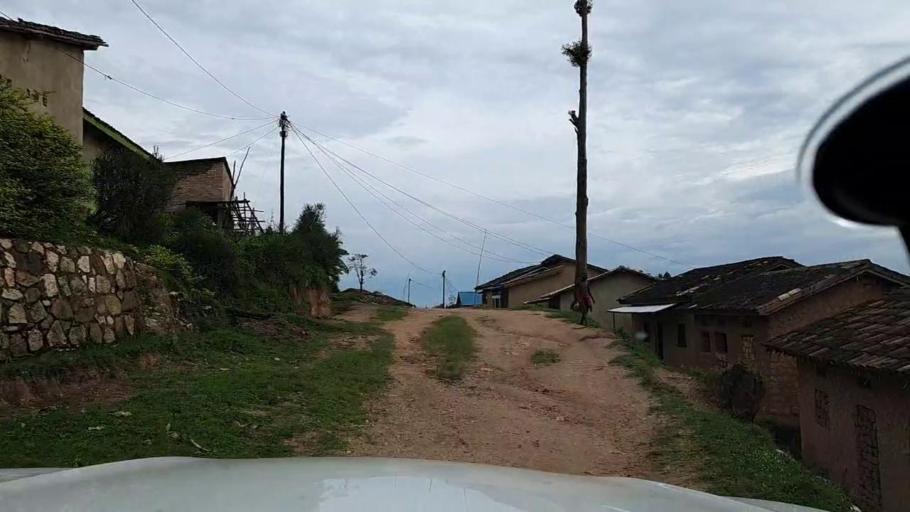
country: RW
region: Southern Province
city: Gitarama
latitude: -2.1277
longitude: 29.6560
